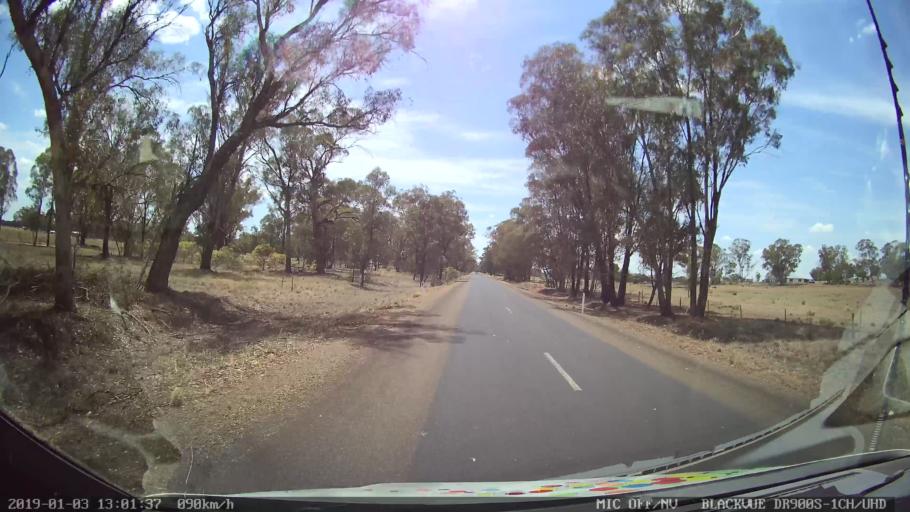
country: AU
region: New South Wales
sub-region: Cabonne
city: Canowindra
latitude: -33.6229
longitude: 148.4205
